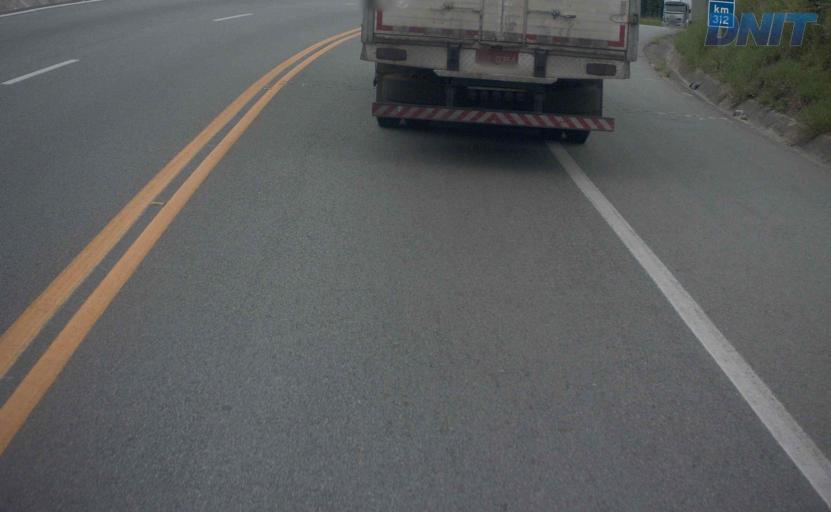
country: BR
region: Minas Gerais
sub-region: Nova Era
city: Nova Era
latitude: -19.6516
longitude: -42.9470
